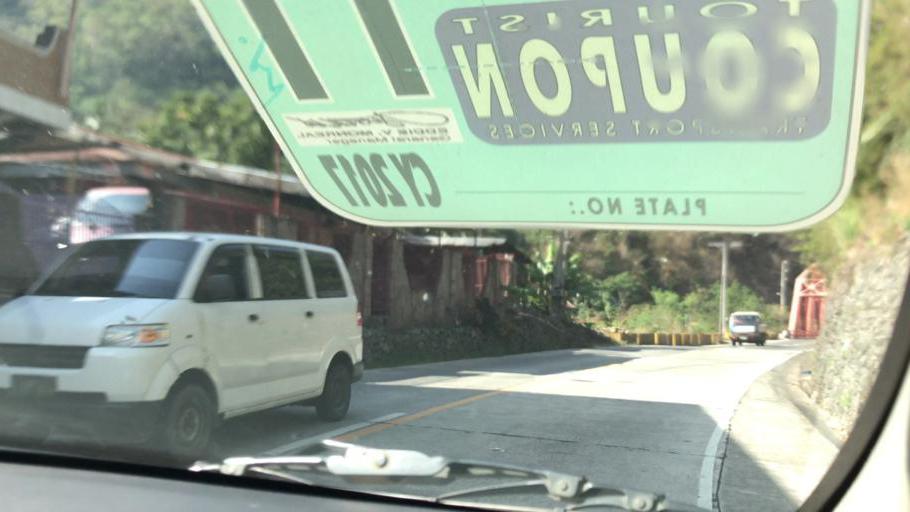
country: PH
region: Cordillera
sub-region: Province of Benguet
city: Tuba
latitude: 16.3192
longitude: 120.6151
